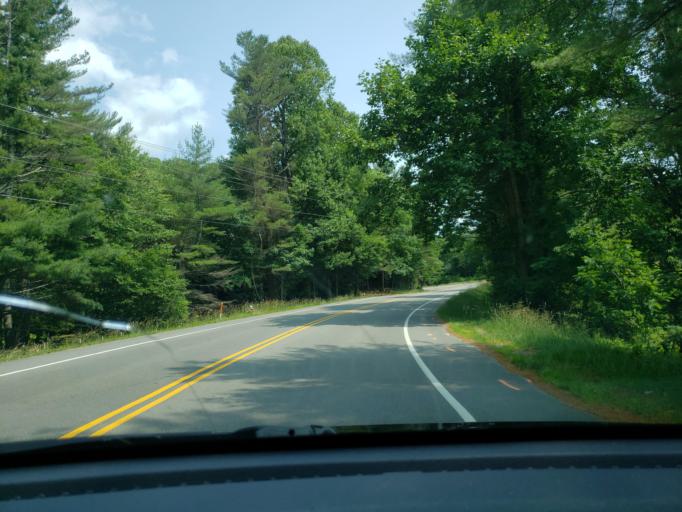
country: US
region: North Carolina
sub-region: Watauga County
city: Blowing Rock
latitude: 36.1383
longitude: -81.6856
